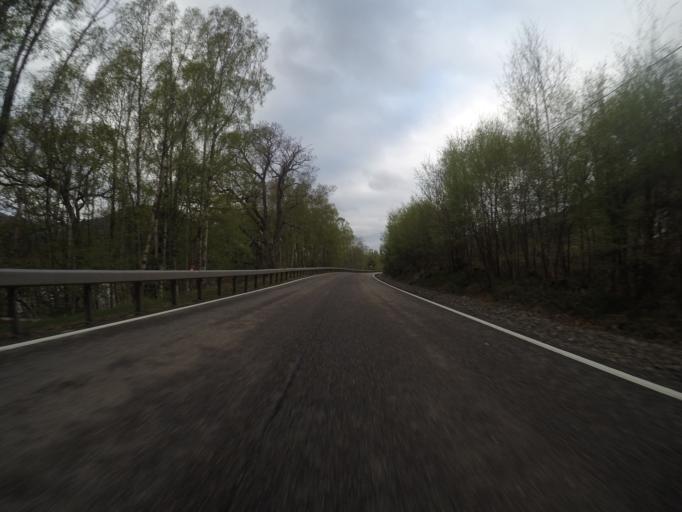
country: GB
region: Scotland
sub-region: Highland
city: Kingussie
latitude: 56.9575
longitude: -4.4707
